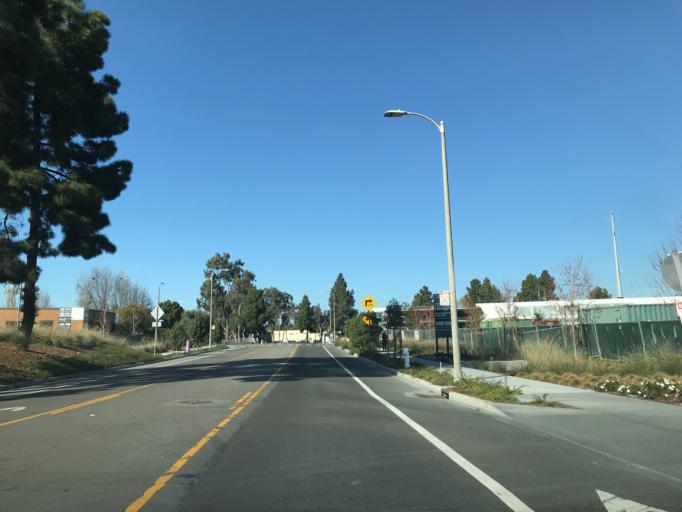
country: US
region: California
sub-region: Santa Clara County
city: Sunnyvale
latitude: 37.4069
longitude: -122.0232
